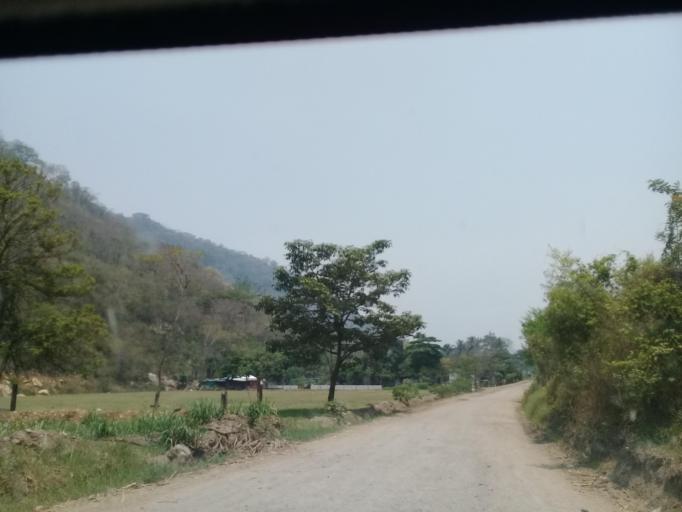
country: MX
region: Veracruz
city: Tezonapa
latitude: 18.6186
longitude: -96.6956
